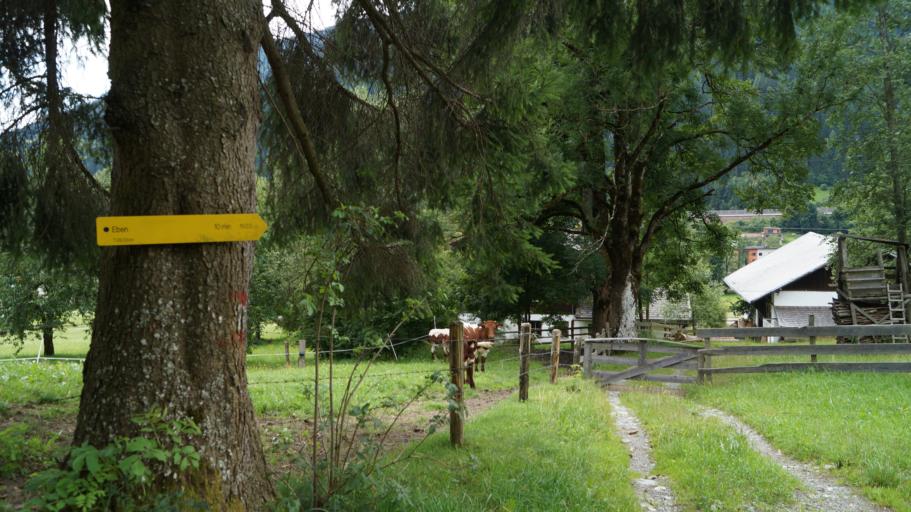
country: AT
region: Salzburg
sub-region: Politischer Bezirk Sankt Johann im Pongau
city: Eben im Pongau
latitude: 47.4058
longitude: 13.4008
